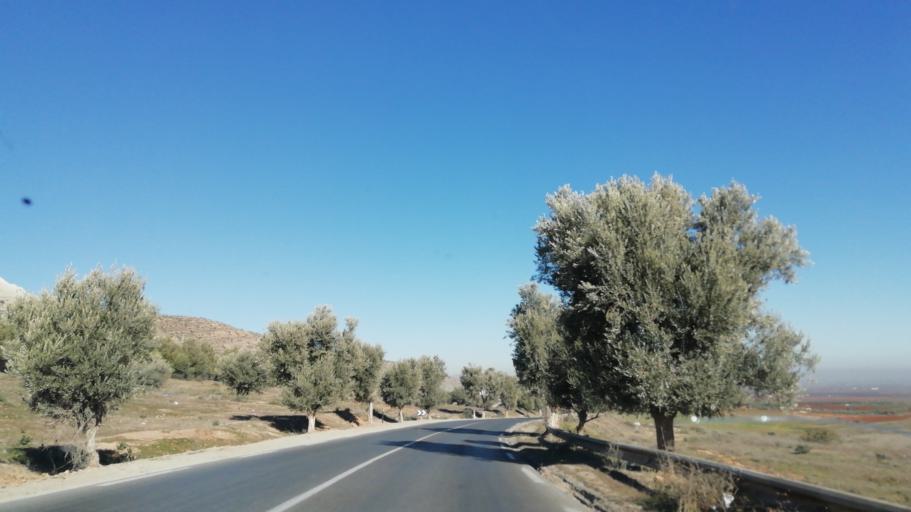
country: DZ
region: Mascara
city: Mascara
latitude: 35.2474
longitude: 0.1209
